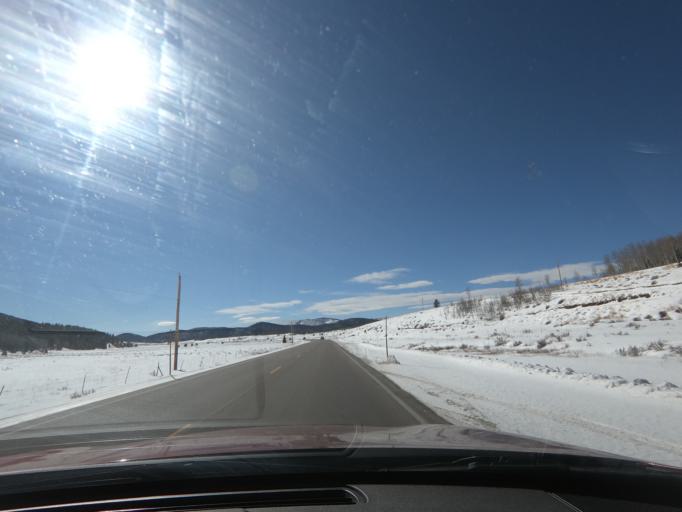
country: US
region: Colorado
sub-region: Teller County
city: Cripple Creek
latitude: 38.7938
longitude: -105.1240
